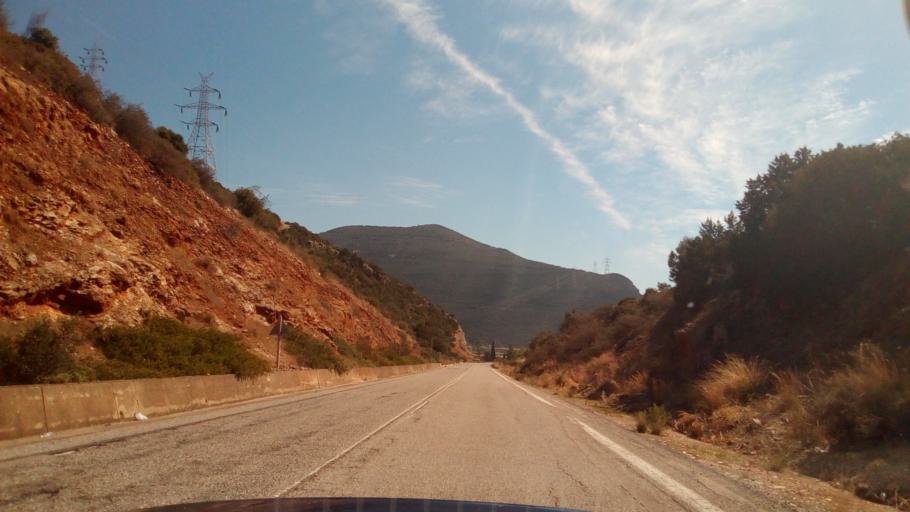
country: GR
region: West Greece
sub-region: Nomos Achaias
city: Selianitika
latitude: 38.3688
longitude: 22.1122
